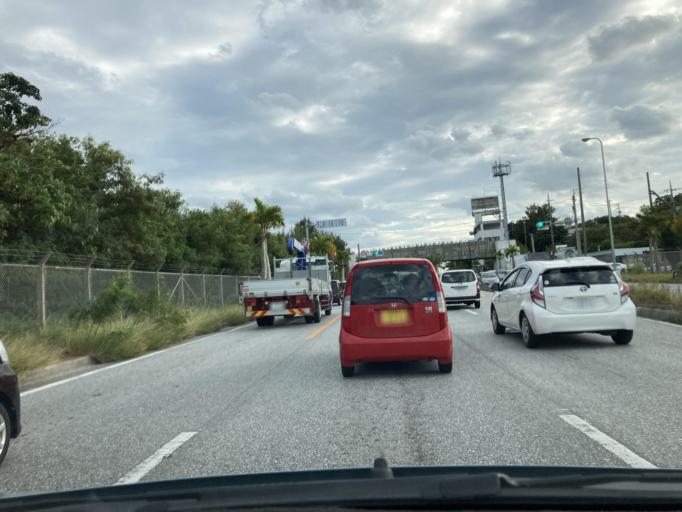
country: JP
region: Okinawa
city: Chatan
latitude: 26.3373
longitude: 127.7515
